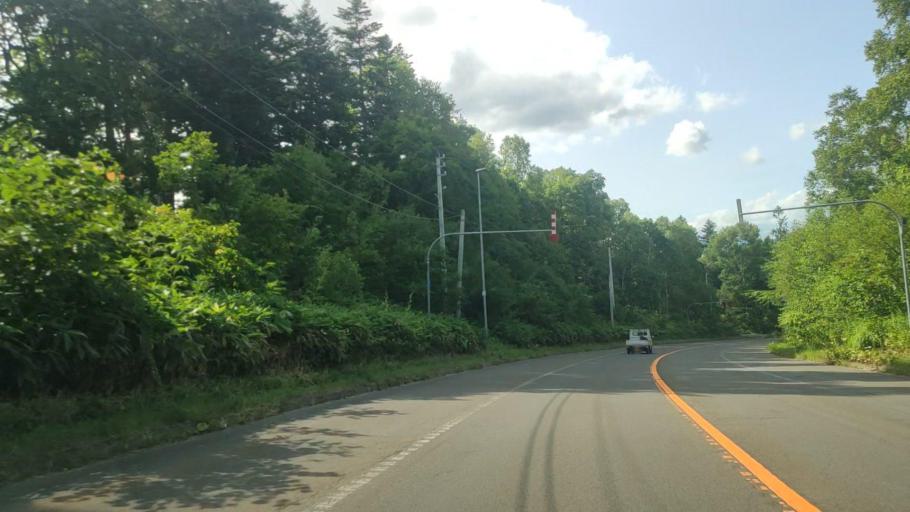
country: JP
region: Hokkaido
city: Nayoro
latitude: 44.3862
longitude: 142.3988
